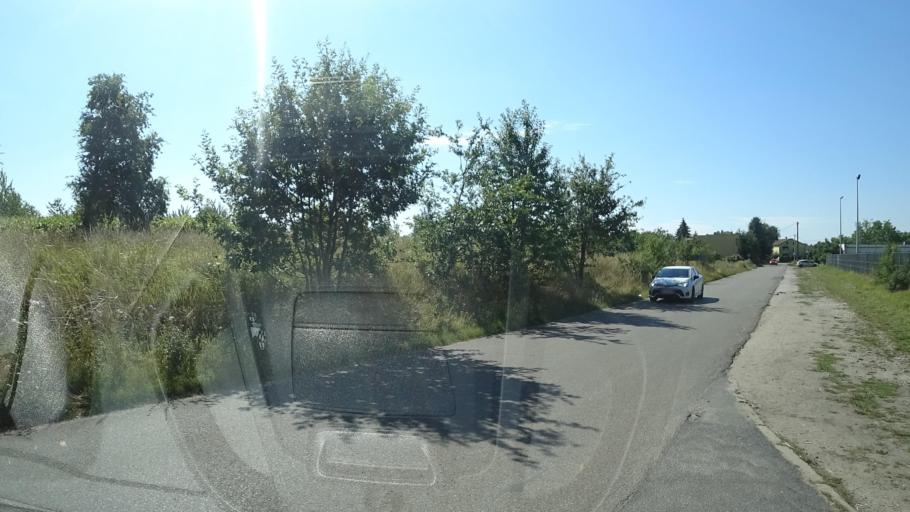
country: PL
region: Greater Poland Voivodeship
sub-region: Powiat koninski
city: Slesin
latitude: 52.3745
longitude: 18.3225
